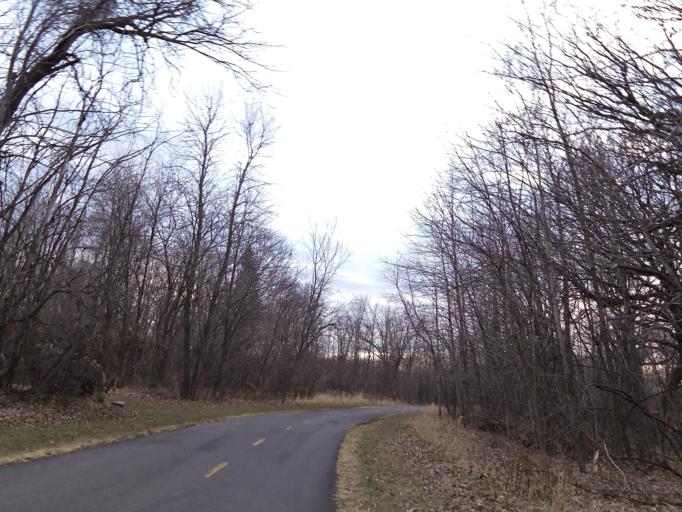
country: US
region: Minnesota
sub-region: Scott County
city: Prior Lake
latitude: 44.6967
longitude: -93.3972
